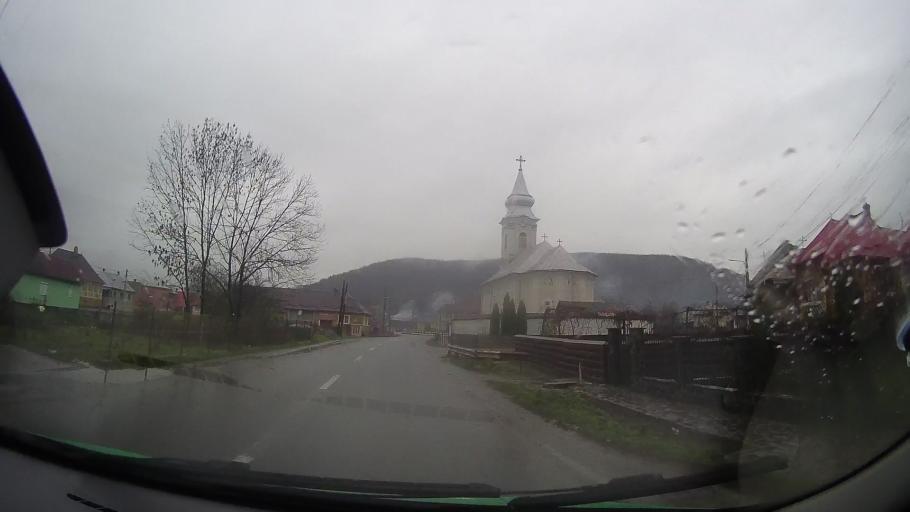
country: RO
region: Bistrita-Nasaud
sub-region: Comuna Sieut
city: Sieut
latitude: 46.9760
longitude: 24.6490
